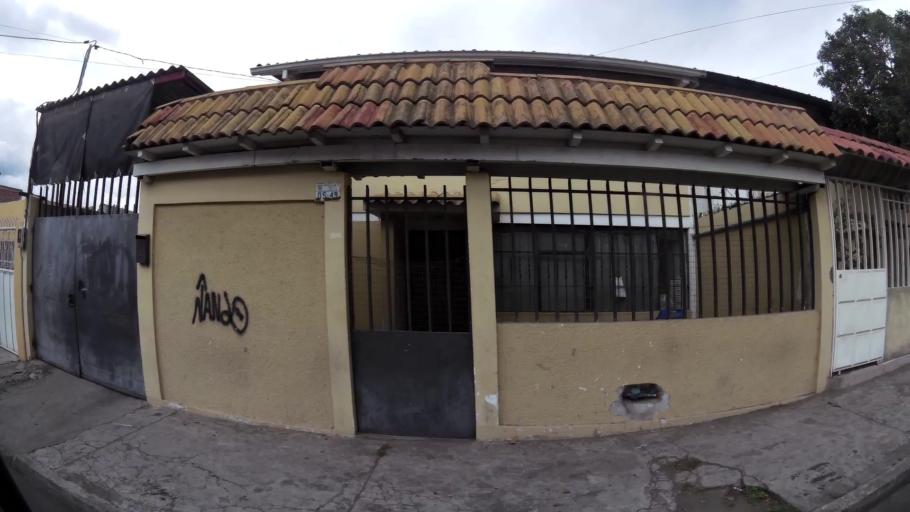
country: EC
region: Tungurahua
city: Ambato
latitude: -1.2601
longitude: -78.6385
